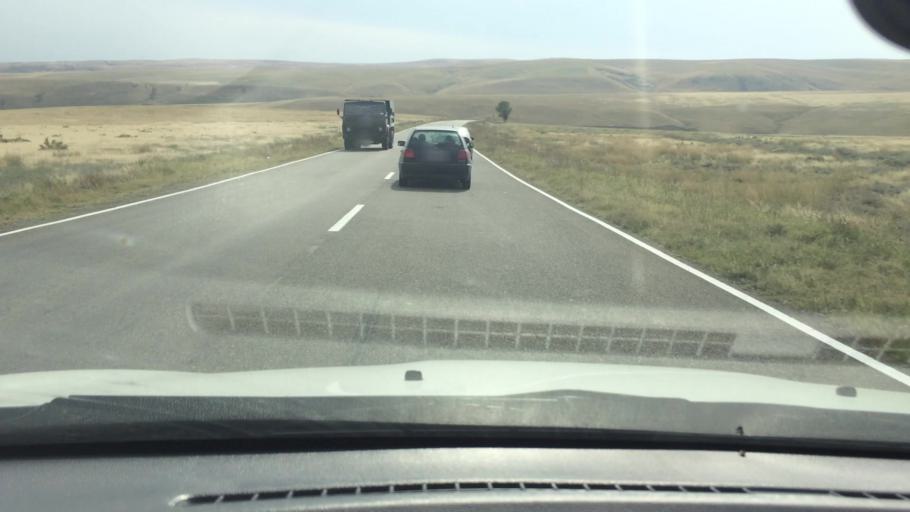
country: GE
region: Kvemo Kartli
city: Rust'avi
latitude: 41.5278
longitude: 44.9388
